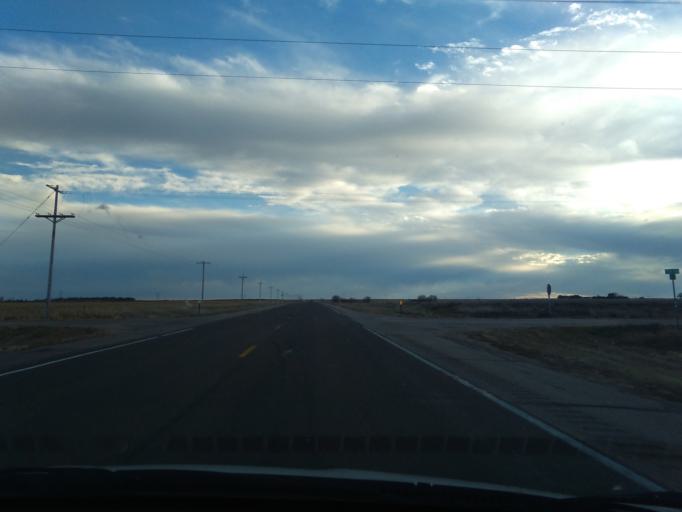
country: US
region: Nebraska
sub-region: Phelps County
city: Holdrege
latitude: 40.3946
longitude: -99.3699
